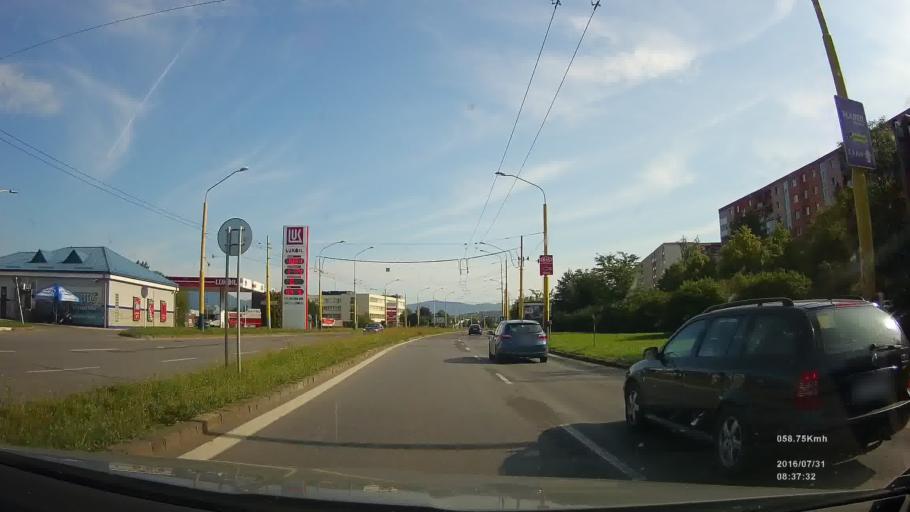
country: SK
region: Presovsky
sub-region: Okres Presov
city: Presov
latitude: 48.9915
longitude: 21.2661
